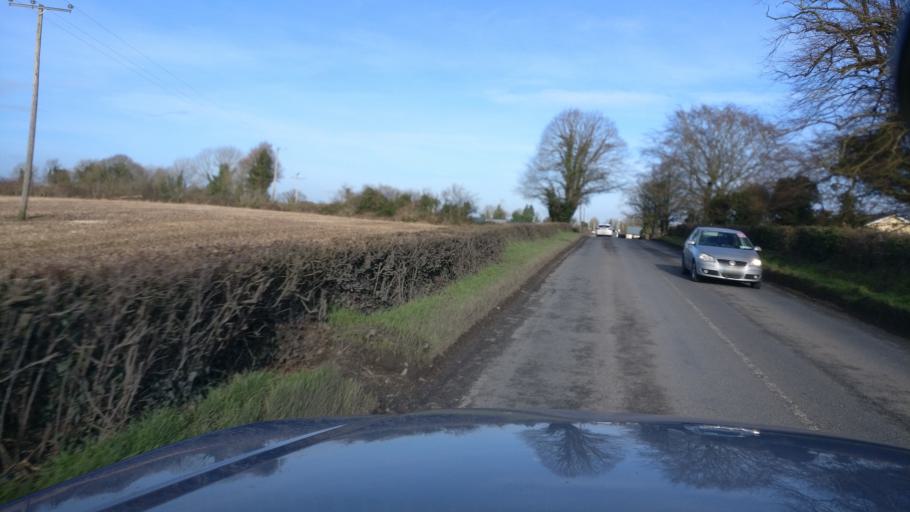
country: IE
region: Leinster
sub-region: Laois
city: Portlaoise
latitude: 53.0225
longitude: -7.2713
